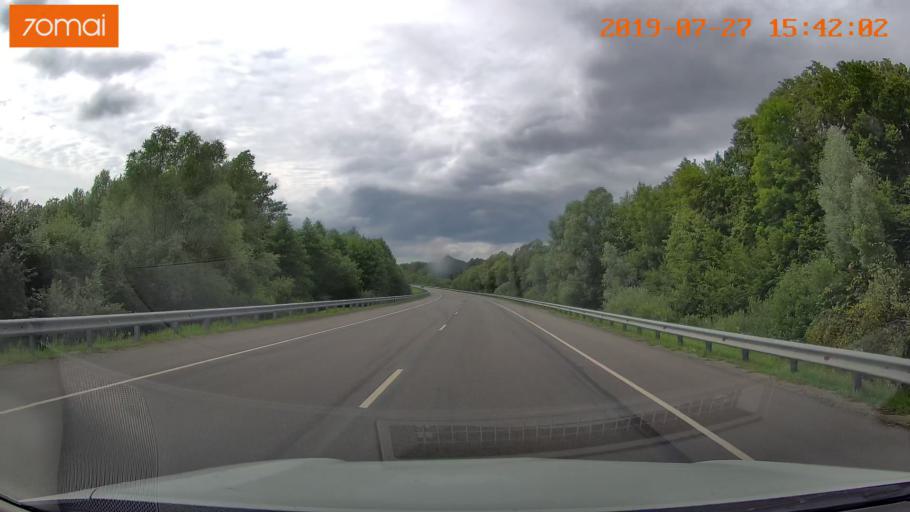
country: RU
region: Kaliningrad
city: Gusev
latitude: 54.6175
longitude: 22.2256
